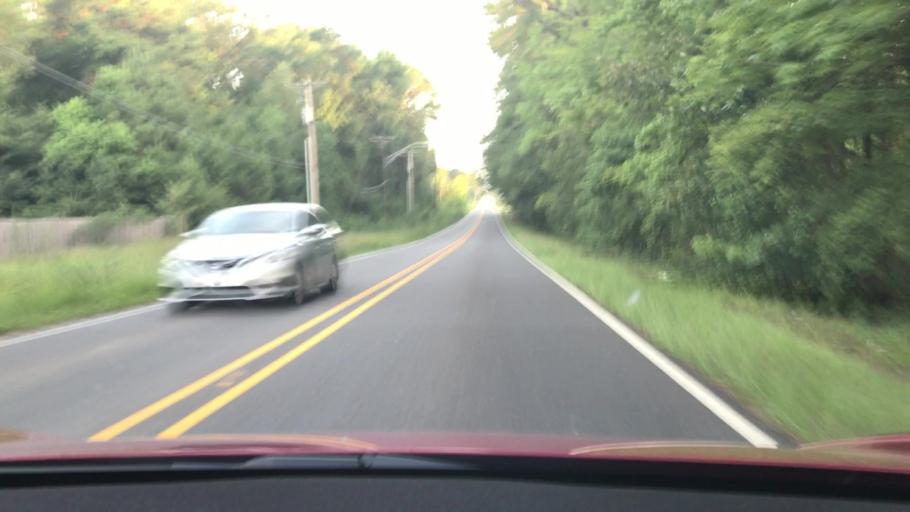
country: US
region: Louisiana
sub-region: Bossier Parish
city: Bossier City
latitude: 32.3961
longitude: -93.7634
